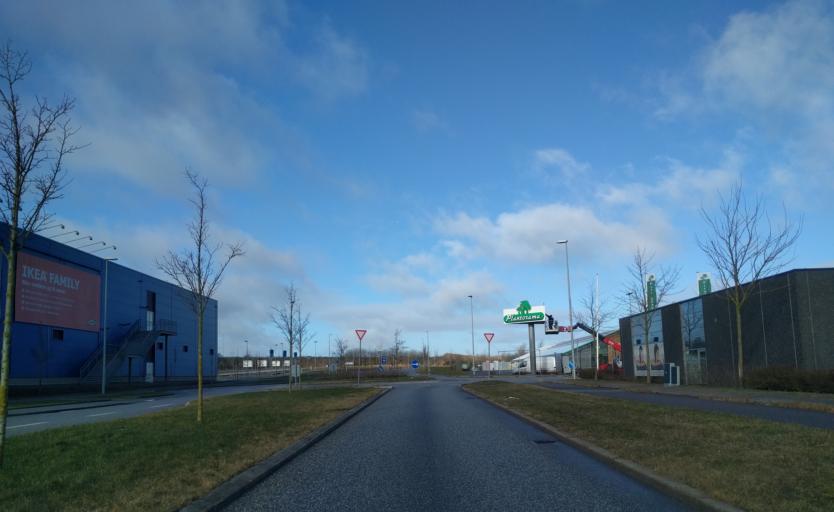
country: DK
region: North Denmark
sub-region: Alborg Kommune
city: Svenstrup
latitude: 56.9967
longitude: 9.8667
